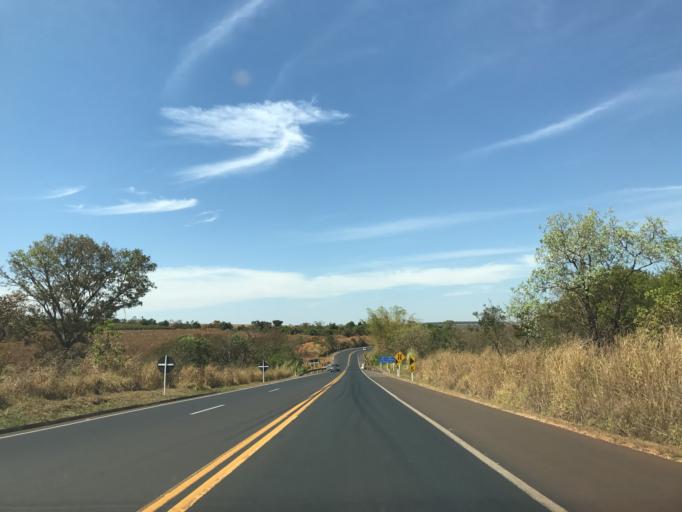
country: BR
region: Minas Gerais
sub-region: Monte Alegre De Minas
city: Monte Alegre de Minas
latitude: -19.0256
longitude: -49.0118
